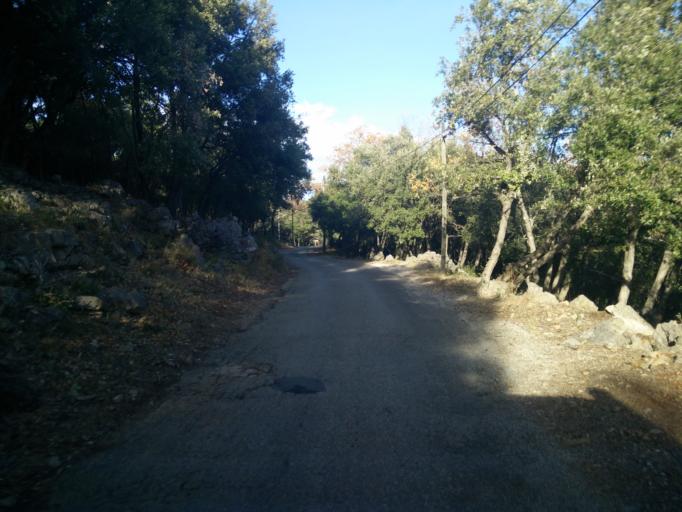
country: FR
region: Provence-Alpes-Cote d'Azur
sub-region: Departement du Var
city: Belgentier
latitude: 43.2114
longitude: 5.9836
